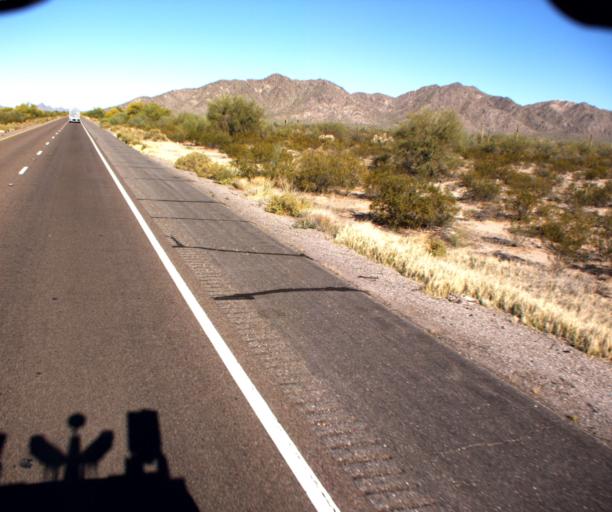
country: US
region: Arizona
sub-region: Maricopa County
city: Gila Bend
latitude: 32.8556
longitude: -112.3760
